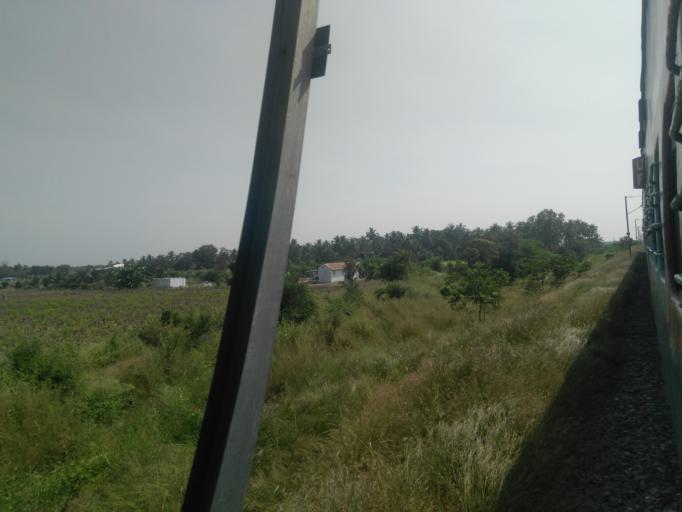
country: IN
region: Tamil Nadu
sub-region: Coimbatore
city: Periyanayakkanpalaiyam
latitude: 11.1360
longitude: 76.9487
